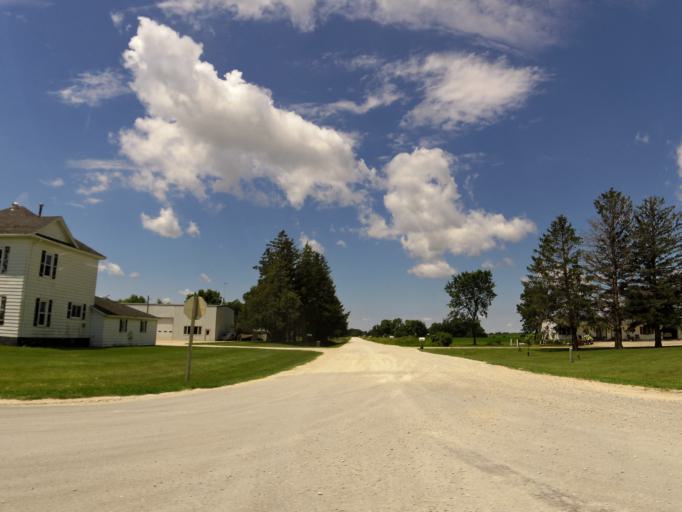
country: US
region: Iowa
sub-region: Fayette County
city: Oelwein
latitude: 42.7004
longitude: -91.9132
